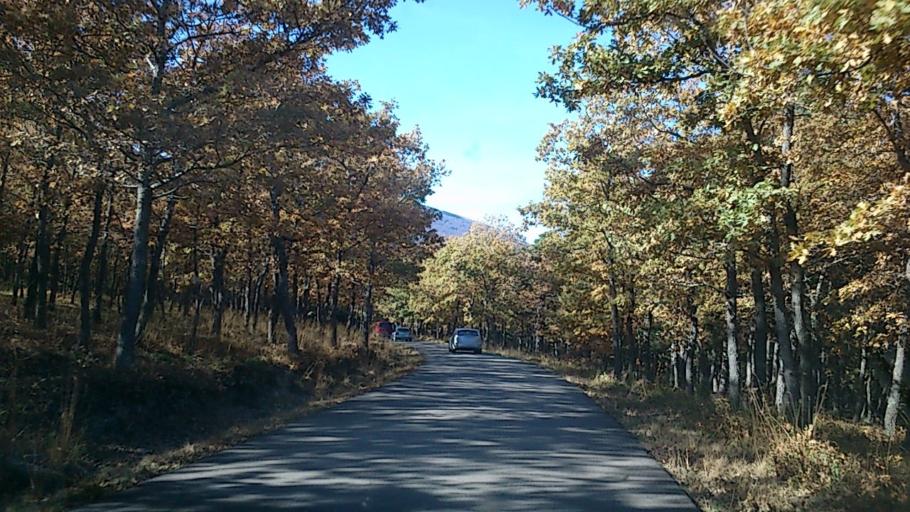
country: ES
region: Aragon
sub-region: Provincia de Zaragoza
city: Lituenigo
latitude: 41.8104
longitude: -1.8067
